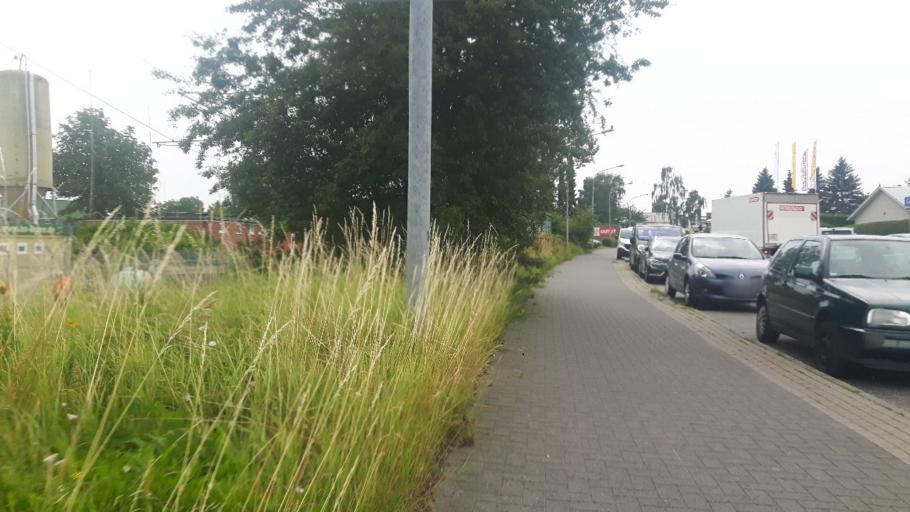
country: DE
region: Schleswig-Holstein
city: Luebeck
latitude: 53.8878
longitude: 10.6909
